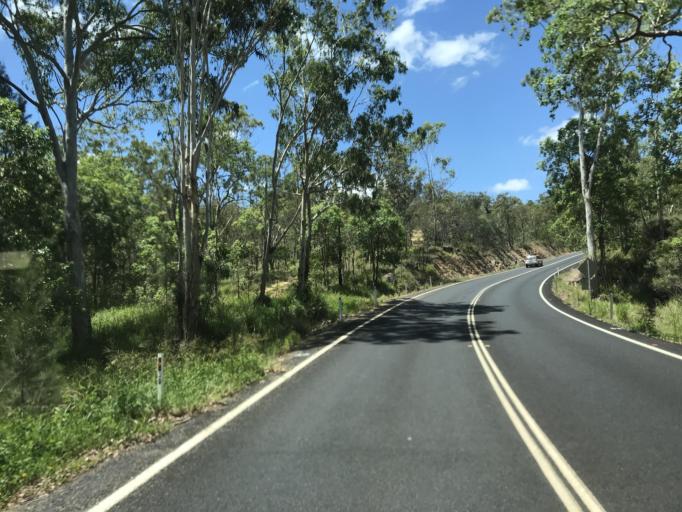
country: AU
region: Queensland
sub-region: Tablelands
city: Atherton
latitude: -17.4019
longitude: 145.3899
